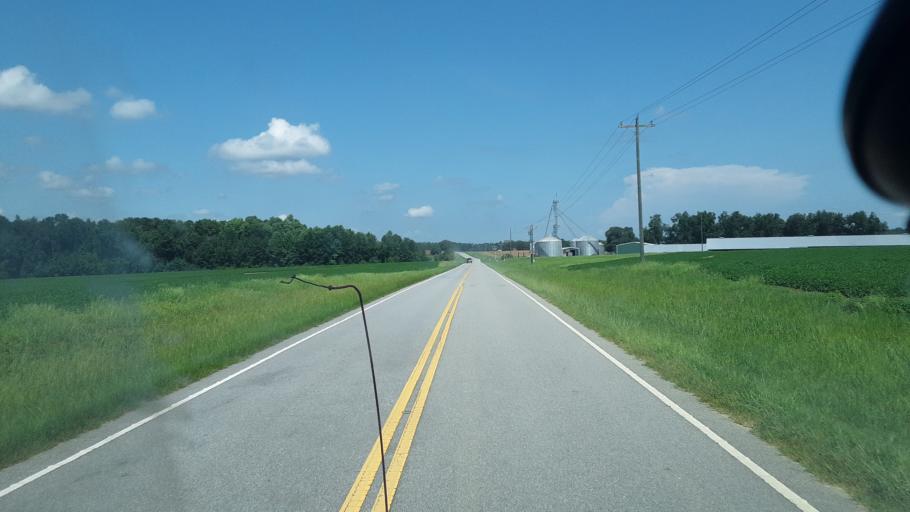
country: US
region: South Carolina
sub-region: Orangeburg County
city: Edisto
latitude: 33.4406
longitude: -81.0177
